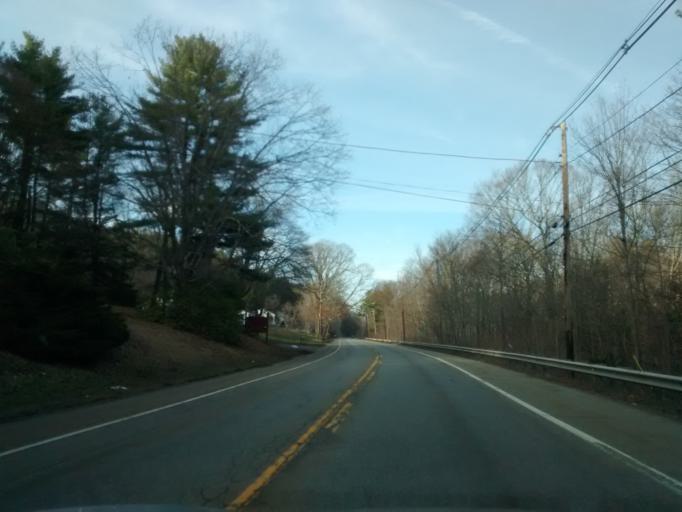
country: US
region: Massachusetts
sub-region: Worcester County
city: Charlton
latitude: 42.1344
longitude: -72.0010
